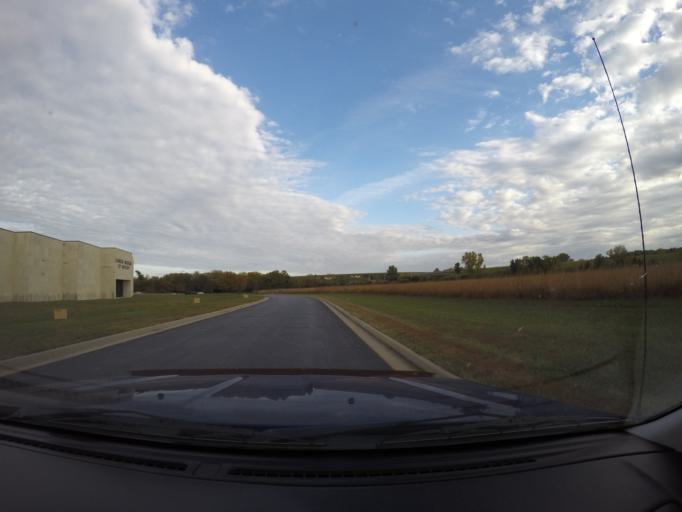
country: US
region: Kansas
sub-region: Shawnee County
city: Silver Lake
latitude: 39.0556
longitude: -95.7764
